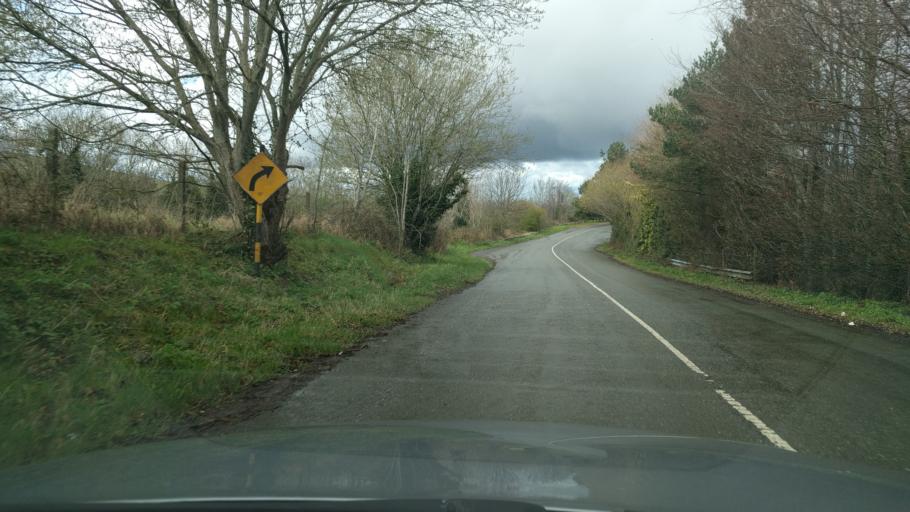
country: IE
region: Leinster
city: Oldbawn
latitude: 53.2499
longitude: -6.3618
